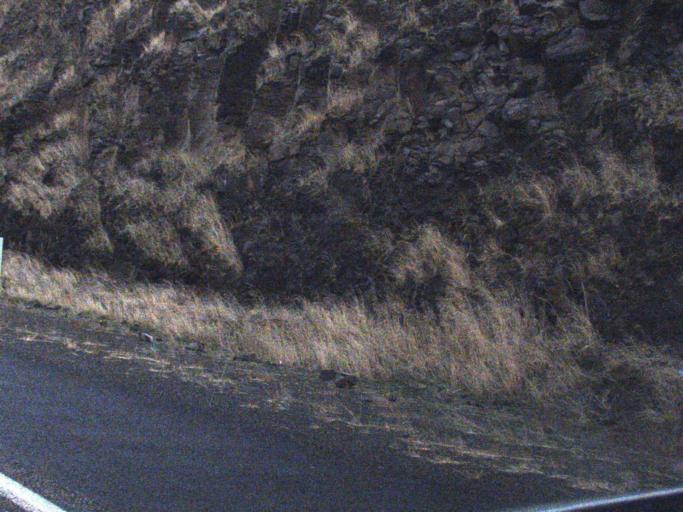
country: US
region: Washington
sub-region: Columbia County
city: Dayton
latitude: 46.4274
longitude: -117.9467
